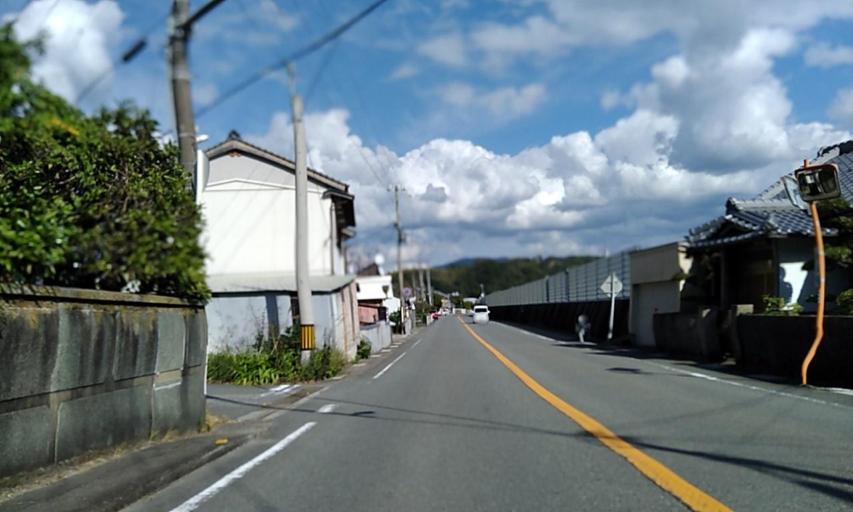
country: JP
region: Wakayama
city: Tanabe
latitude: 33.7466
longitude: 135.3459
